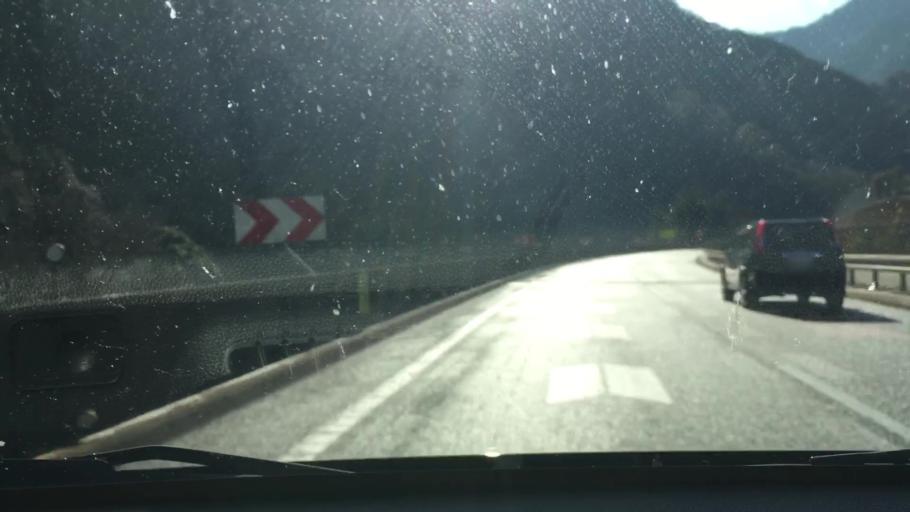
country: JP
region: Kumamoto
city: Hitoyoshi
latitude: 32.3181
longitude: 130.7558
